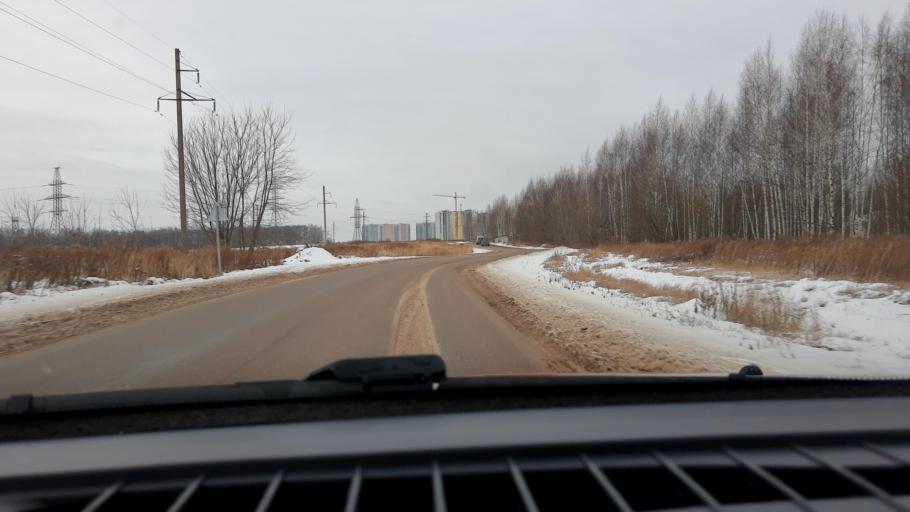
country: RU
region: Nizjnij Novgorod
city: Afonino
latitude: 56.2446
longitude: 44.0728
